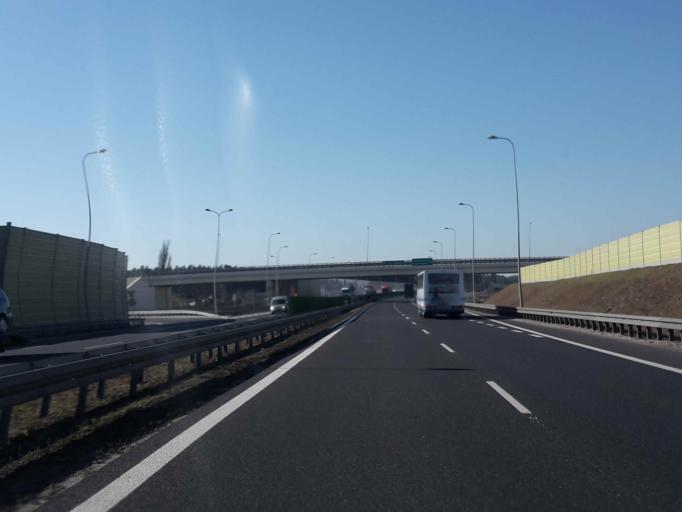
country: PL
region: Greater Poland Voivodeship
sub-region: Powiat gnieznienski
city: Lubowo
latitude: 52.4575
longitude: 17.3883
